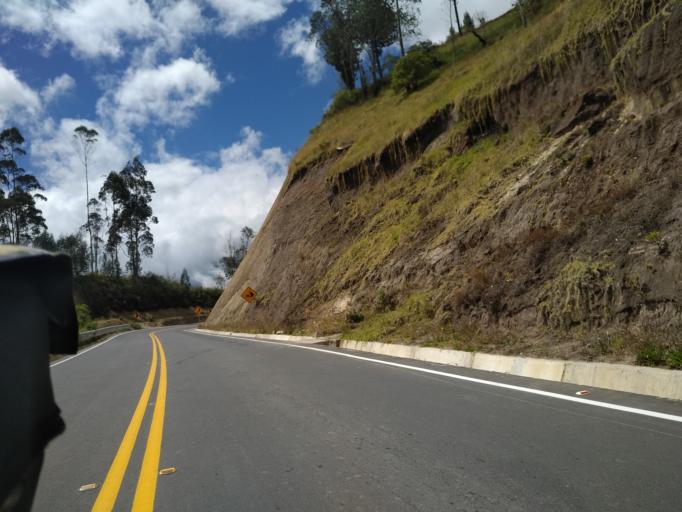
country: EC
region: Cotopaxi
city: Saquisili
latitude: -0.7298
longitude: -78.8964
